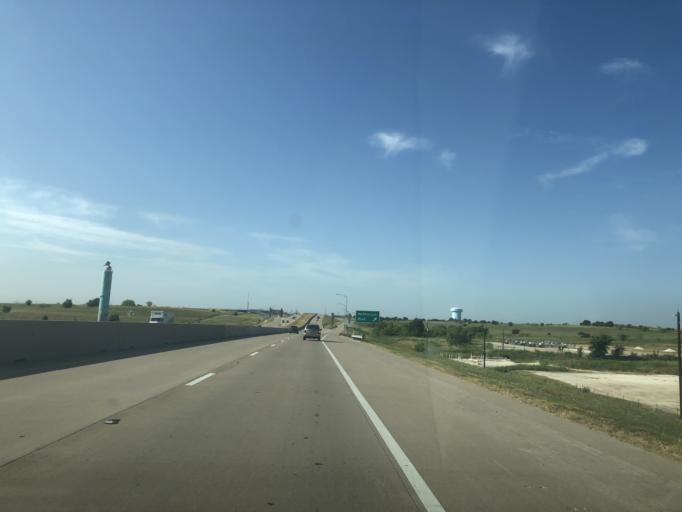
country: US
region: Texas
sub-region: Tarrant County
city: Crowley
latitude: 32.6148
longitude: -97.4127
